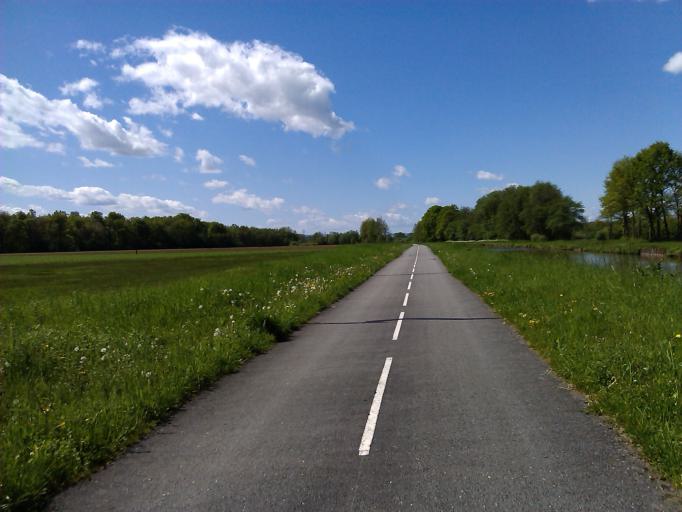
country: FR
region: Franche-Comte
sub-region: Territoire de Belfort
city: Morvillars
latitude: 47.5776
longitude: 6.9593
